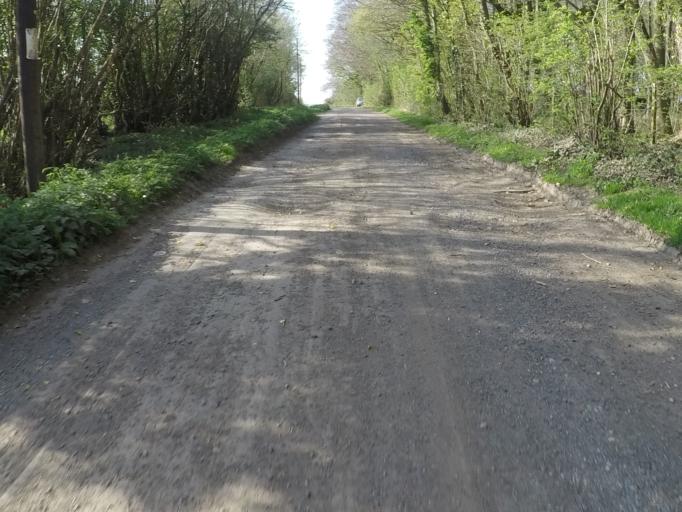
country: GB
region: England
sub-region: Oxfordshire
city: Charlbury
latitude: 51.8912
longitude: -1.4604
